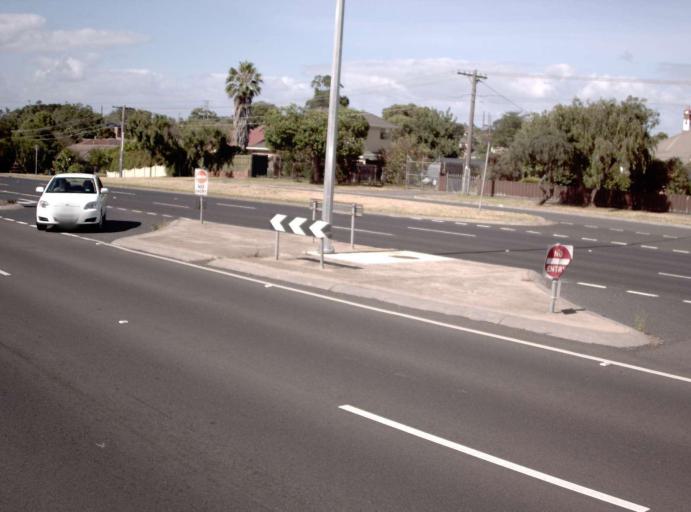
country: AU
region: Victoria
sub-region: Kingston
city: Mordialloc
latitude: -37.9956
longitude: 145.0836
